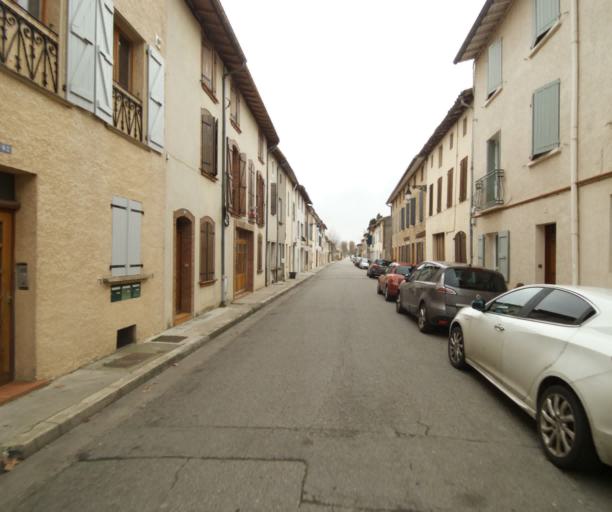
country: FR
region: Midi-Pyrenees
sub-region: Departement de l'Ariege
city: Mazeres
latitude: 43.2506
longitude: 1.6795
